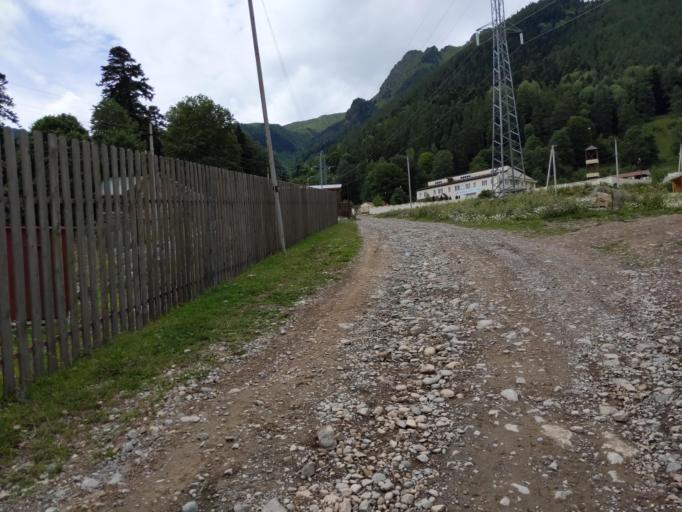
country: RU
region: Karachayevo-Cherkesiya
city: Nizhniy Arkhyz
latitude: 43.5668
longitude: 41.2674
